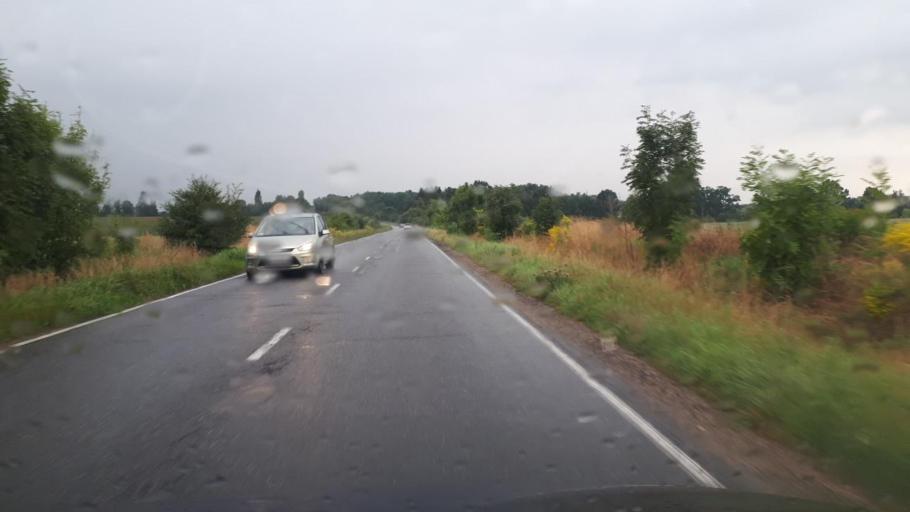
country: PL
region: Silesian Voivodeship
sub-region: Powiat tarnogorski
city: Wieszowa
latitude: 50.3482
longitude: 18.7157
